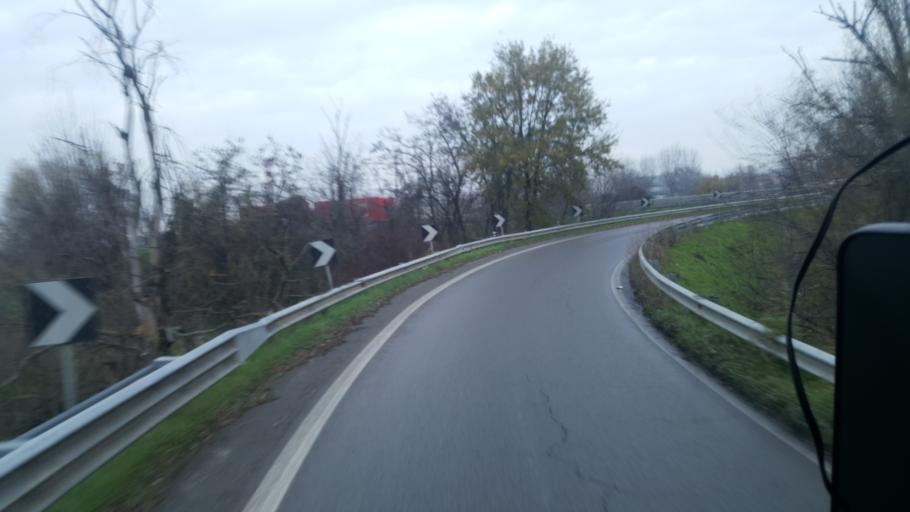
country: IT
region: Emilia-Romagna
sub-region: Provincia di Parma
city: Parma
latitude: 44.8210
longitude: 10.3117
